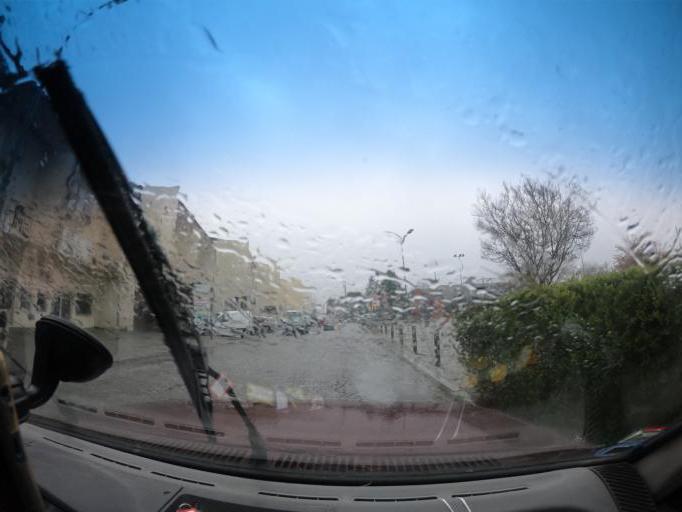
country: PT
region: Guarda
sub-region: Celorico da Beira
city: Celorico da Beira
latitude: 40.6326
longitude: -7.3942
